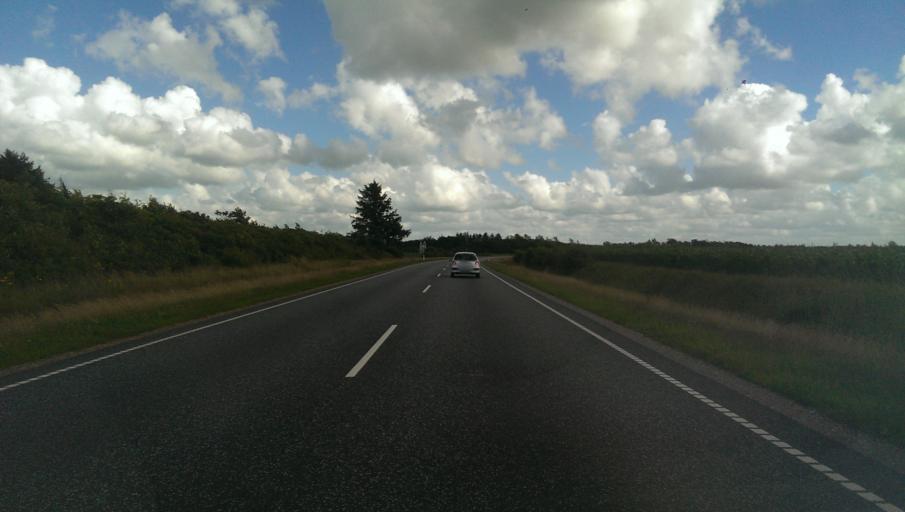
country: DK
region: Central Jutland
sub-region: Ringkobing-Skjern Kommune
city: Tarm
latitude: 55.8981
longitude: 8.5082
